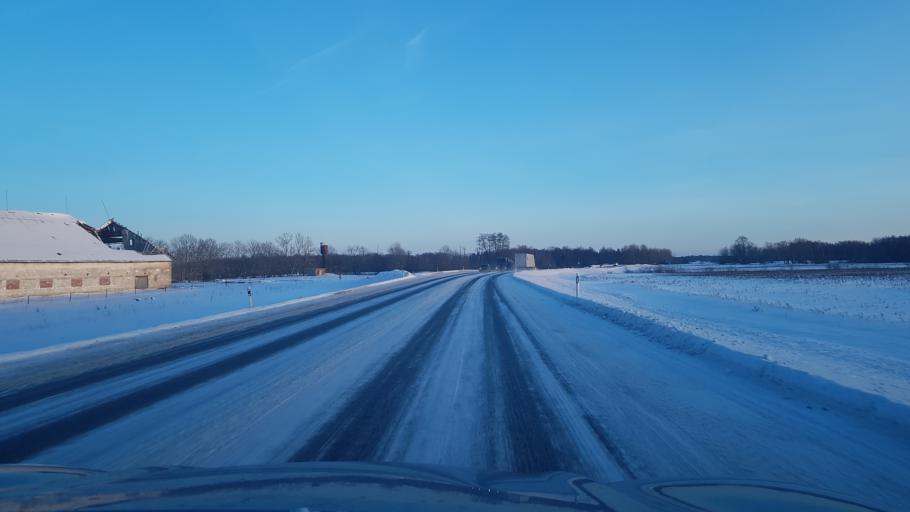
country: EE
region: Ida-Virumaa
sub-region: Narva-Joesuu linn
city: Narva-Joesuu
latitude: 59.3996
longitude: 28.0714
